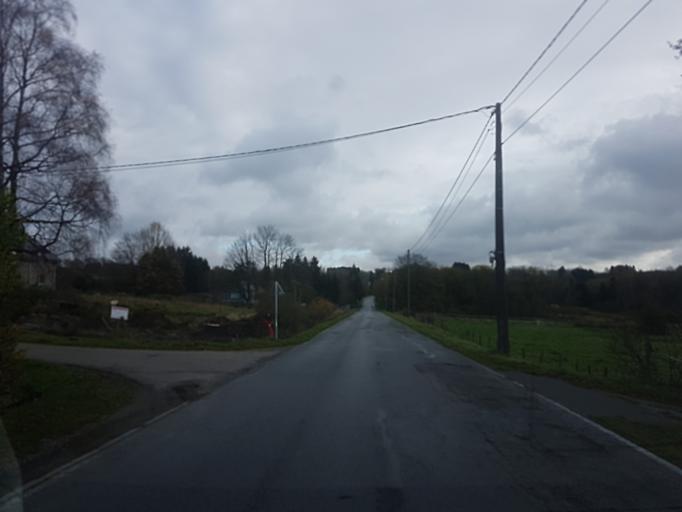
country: BE
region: Wallonia
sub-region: Province de Liege
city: Malmedy
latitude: 50.4809
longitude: 5.9764
